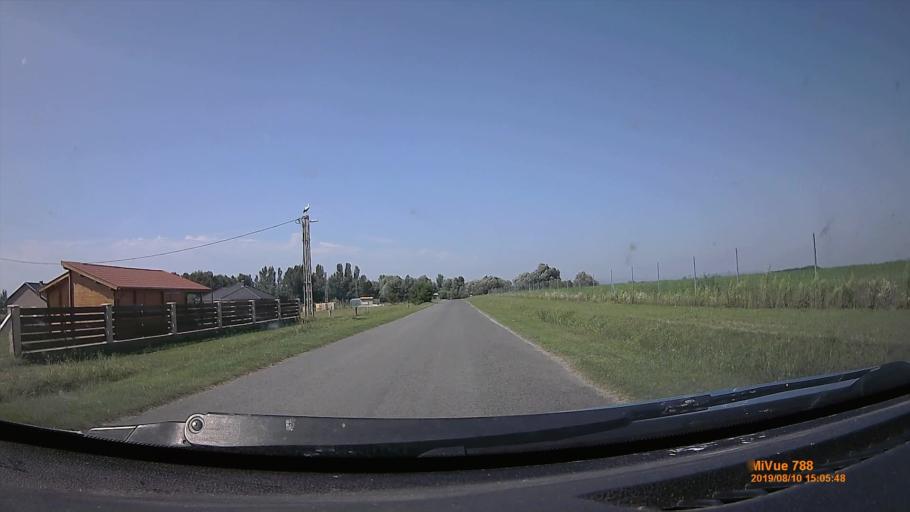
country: HU
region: Somogy
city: Fonyod
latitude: 46.6812
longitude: 17.5645
